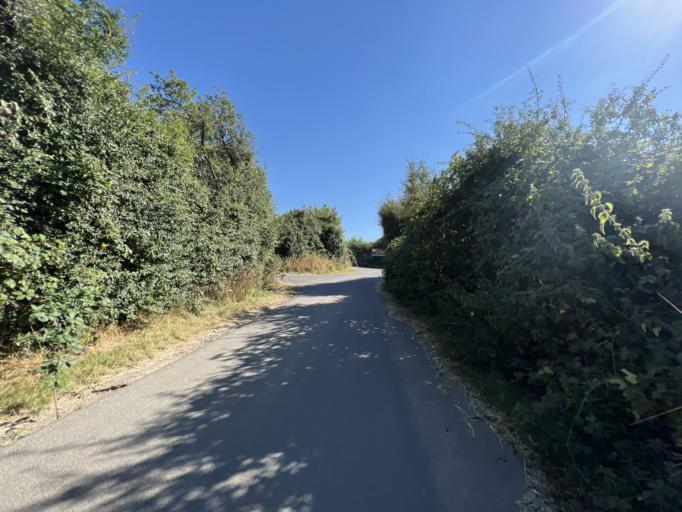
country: DE
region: North Rhine-Westphalia
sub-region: Regierungsbezirk Koln
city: Kreuzau
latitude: 50.7687
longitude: 6.4417
